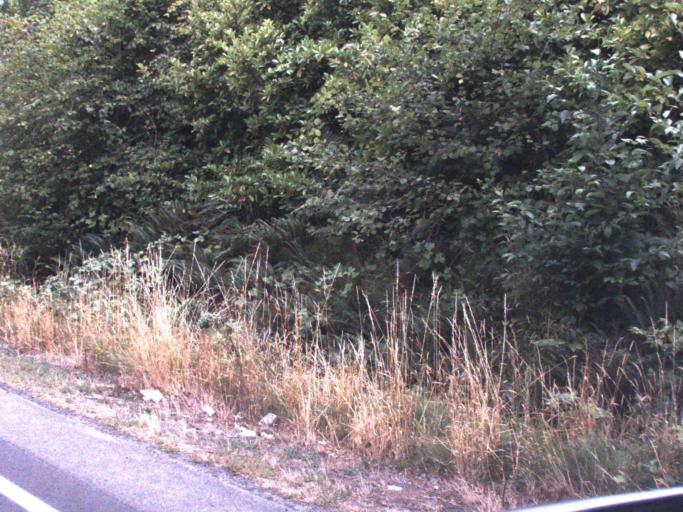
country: US
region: Washington
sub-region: King County
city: Carnation
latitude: 47.6215
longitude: -121.9098
